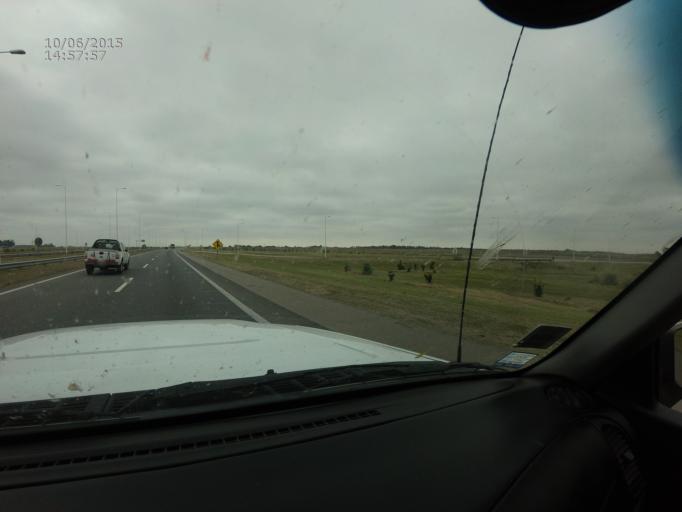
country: AR
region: Cordoba
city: Laguna Larga
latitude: -31.8015
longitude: -63.7300
